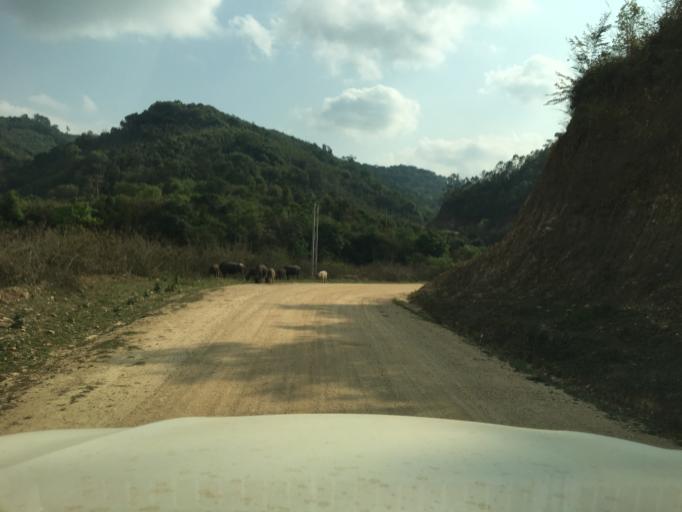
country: LA
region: Houaphan
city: Huameung
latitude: 20.2089
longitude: 103.8553
